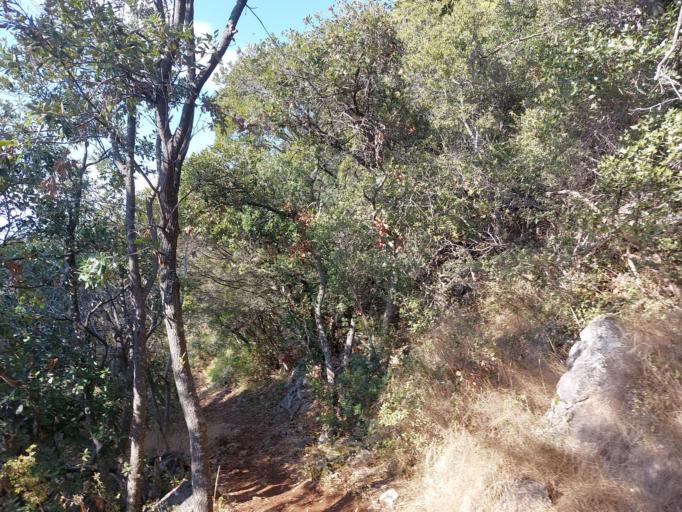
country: HR
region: Dubrovacko-Neretvanska
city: Smokvica
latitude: 42.7655
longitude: 16.8025
